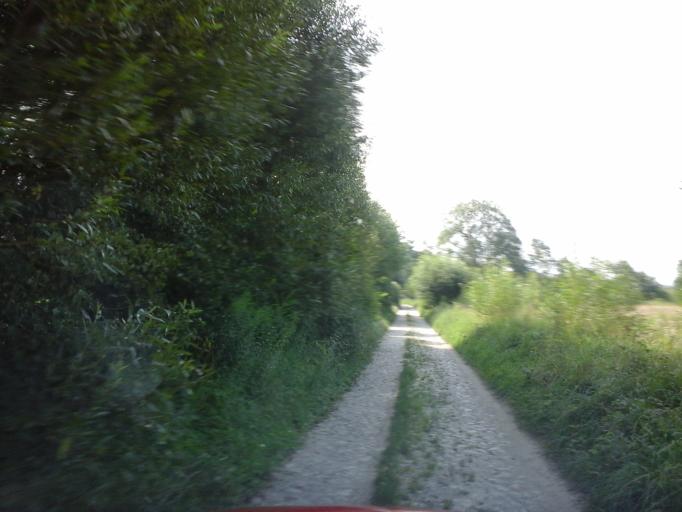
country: PL
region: West Pomeranian Voivodeship
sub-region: Powiat mysliborski
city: Barlinek
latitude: 53.0475
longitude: 15.1980
